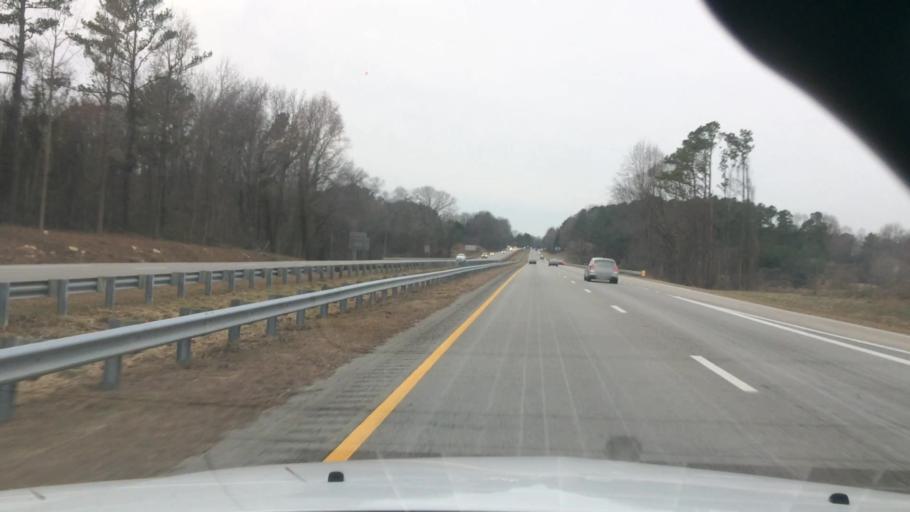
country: US
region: North Carolina
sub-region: Nash County
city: Red Oak
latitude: 35.9803
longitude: -77.9006
